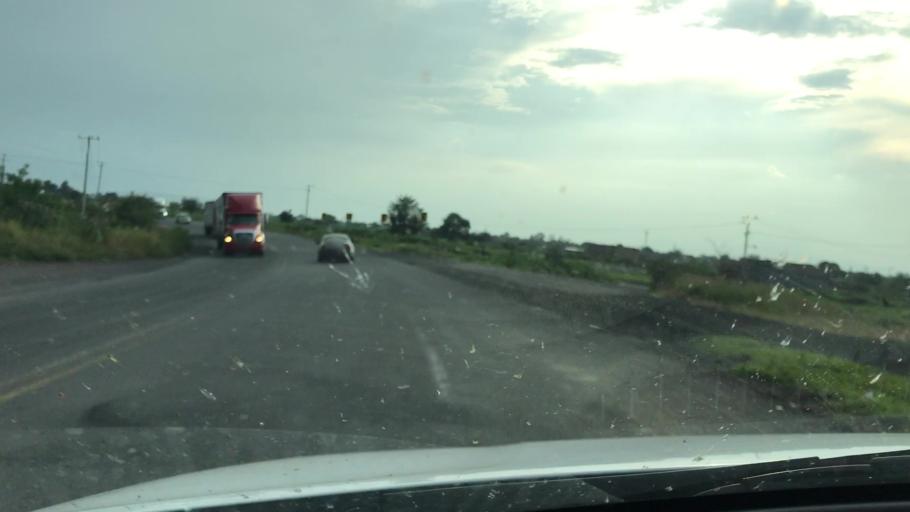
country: MX
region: Michoacan
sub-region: Yurecuaro
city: Yurecuaro
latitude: 20.3290
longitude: -102.2662
